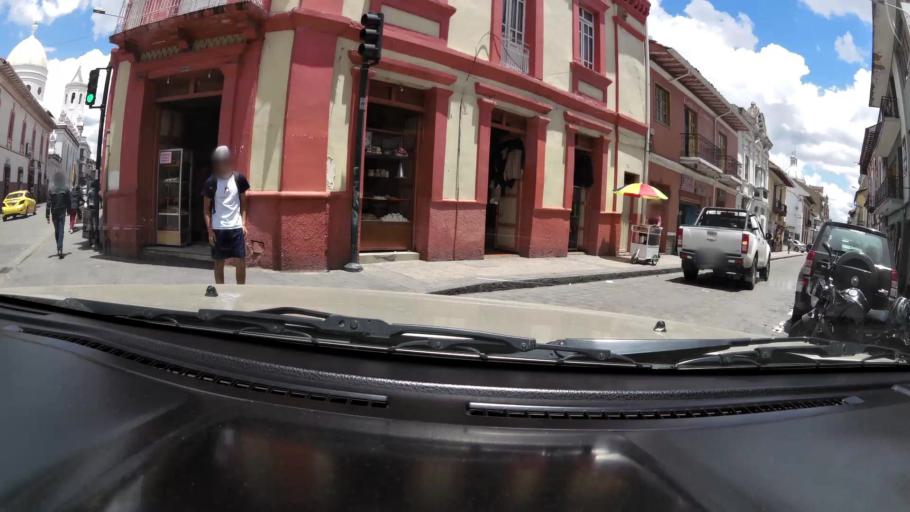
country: EC
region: Azuay
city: Cuenca
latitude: -2.8971
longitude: -79.0078
